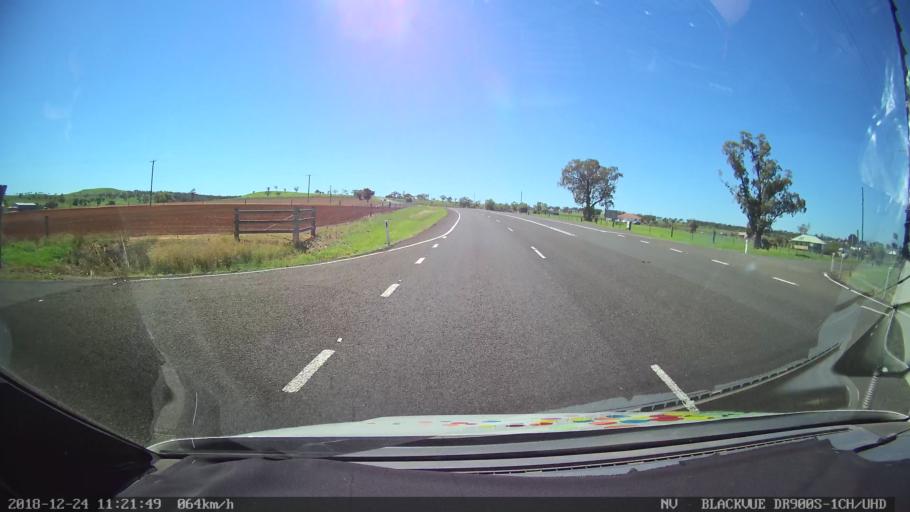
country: AU
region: New South Wales
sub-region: Upper Hunter Shire
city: Merriwa
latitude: -32.1452
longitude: 150.3736
